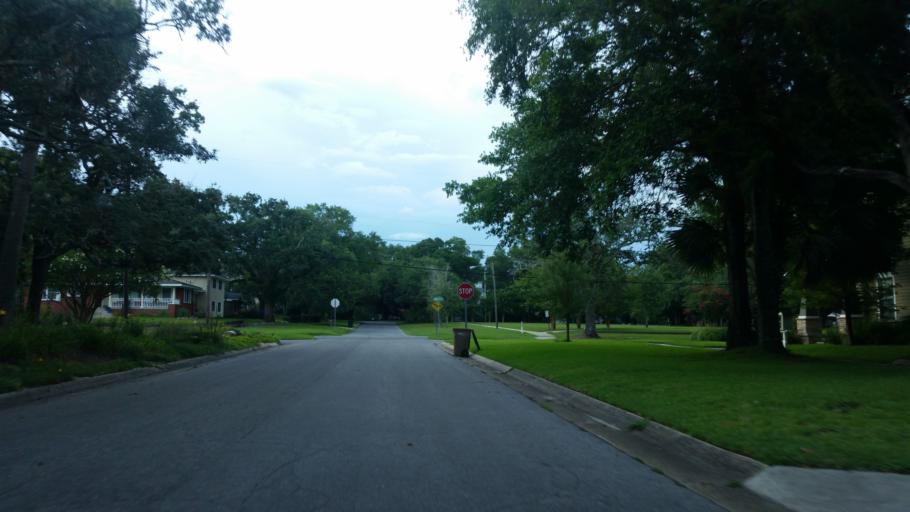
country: US
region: Florida
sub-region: Escambia County
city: Pensacola
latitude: 30.4295
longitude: -87.2070
